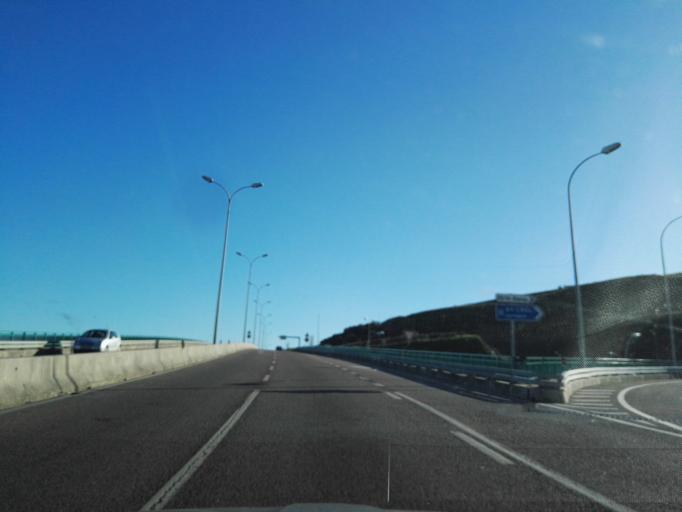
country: PT
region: Lisbon
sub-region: Odivelas
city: Famoes
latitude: 38.7761
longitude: -9.2235
